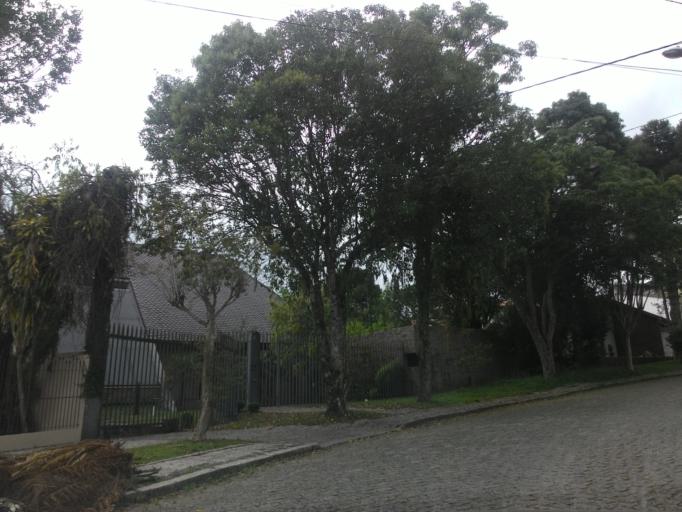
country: BR
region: Parana
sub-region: Curitiba
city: Curitiba
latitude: -25.4611
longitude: -49.2432
